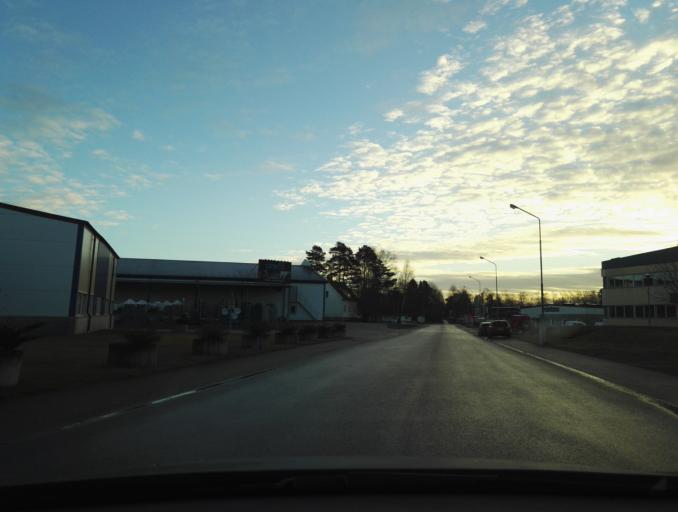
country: SE
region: Kronoberg
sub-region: Vaxjo Kommun
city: Vaexjoe
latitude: 56.8911
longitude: 14.7793
